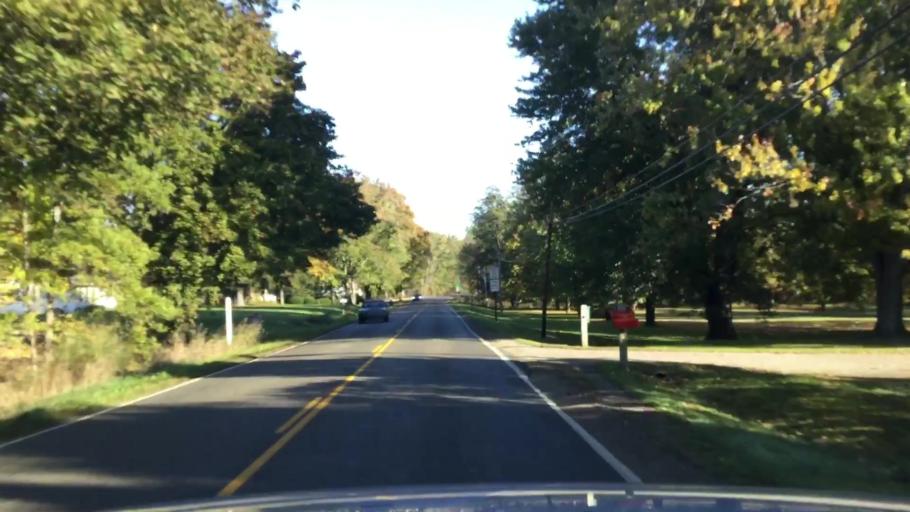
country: US
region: Michigan
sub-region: Genesee County
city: Argentine
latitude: 42.8146
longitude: -83.9438
